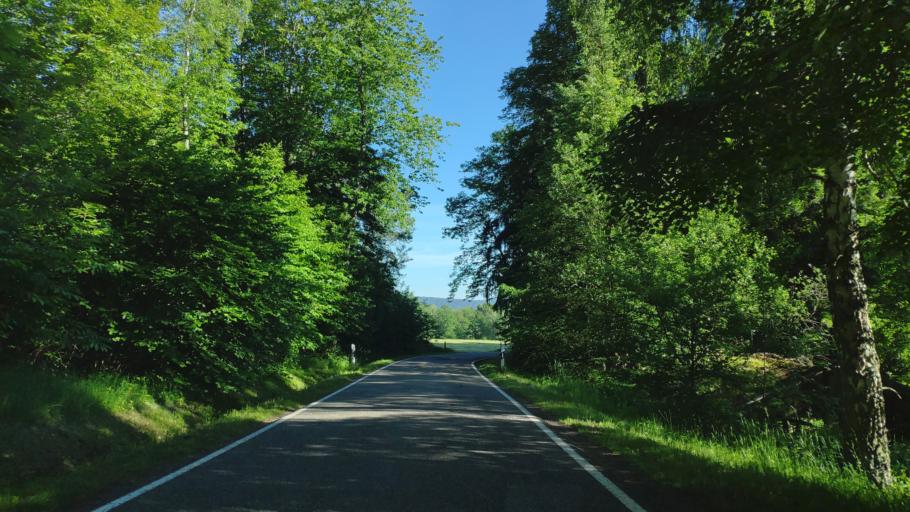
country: DE
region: Rheinland-Pfalz
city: Nothweiler
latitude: 49.0810
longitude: 7.7948
